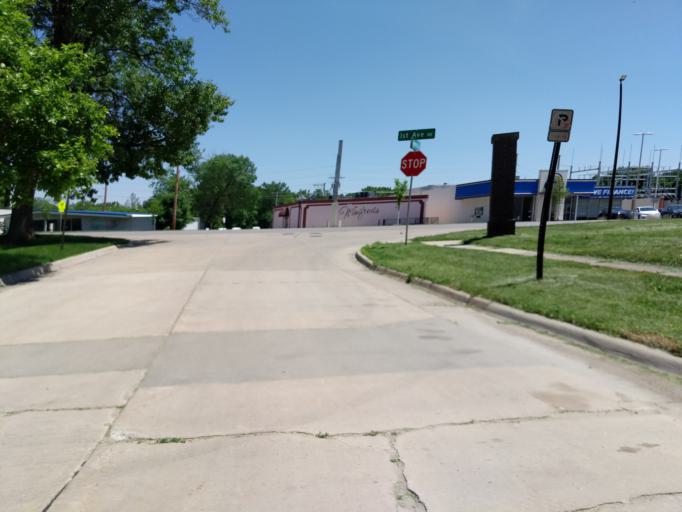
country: US
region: Iowa
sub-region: Linn County
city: Cedar Rapids
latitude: 42.0185
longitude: -91.6341
